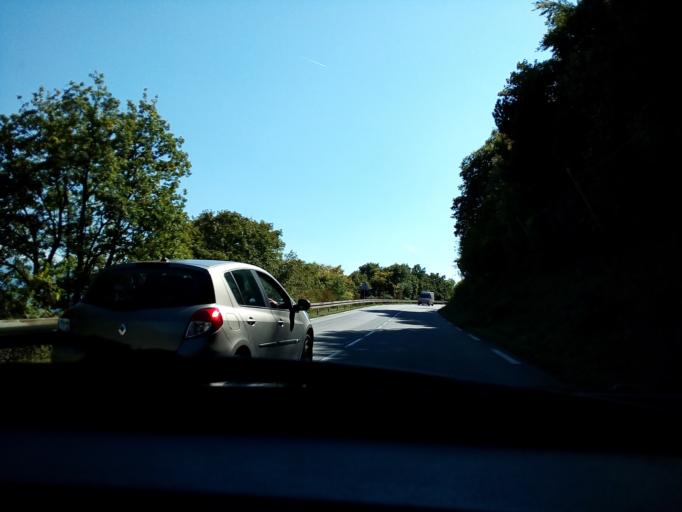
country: FR
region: Rhone-Alpes
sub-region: Departement de l'Isere
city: Sassenage
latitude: 45.2240
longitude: 5.6509
